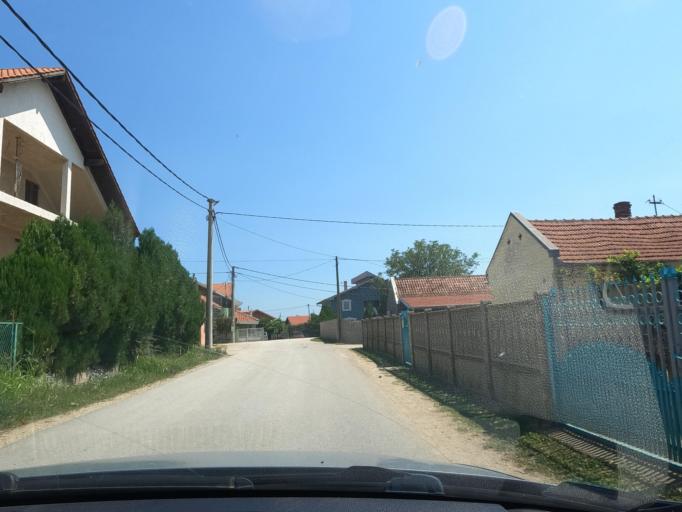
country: RS
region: Central Serbia
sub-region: Branicevski Okrug
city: Pozarevac
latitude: 44.7048
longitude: 21.1645
